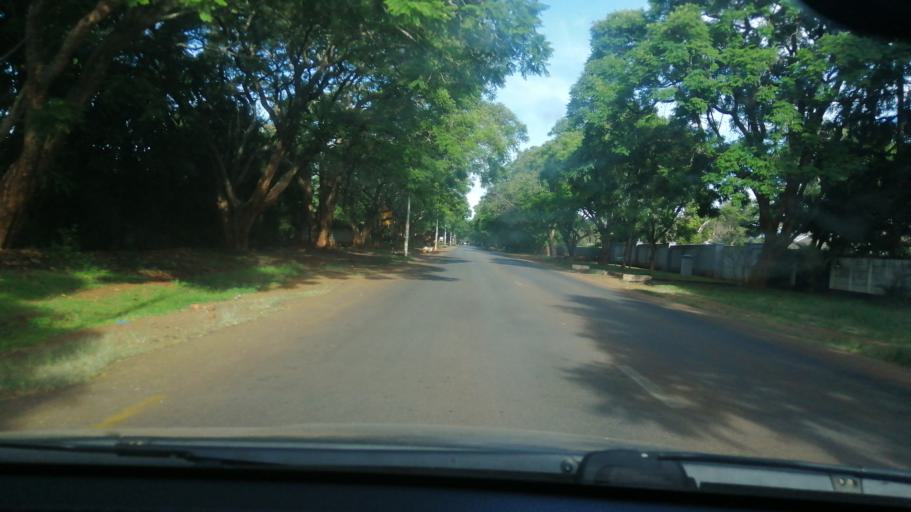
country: ZW
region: Harare
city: Harare
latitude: -17.7626
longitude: 31.0750
